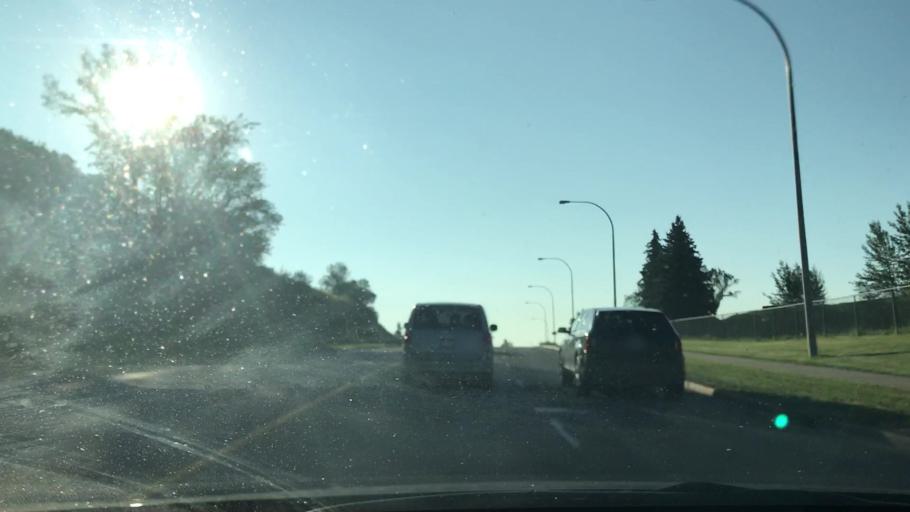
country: CA
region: Alberta
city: Edmonton
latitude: 53.5348
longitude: -113.4540
